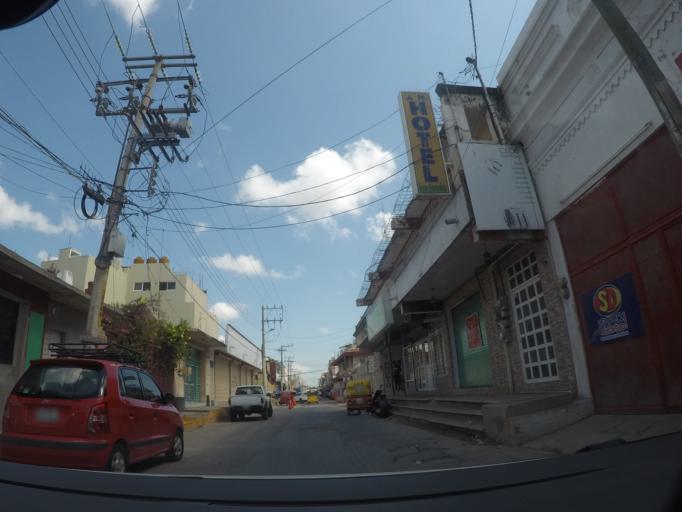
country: MX
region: Oaxaca
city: Juchitan de Zaragoza
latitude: 16.4356
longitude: -95.0211
